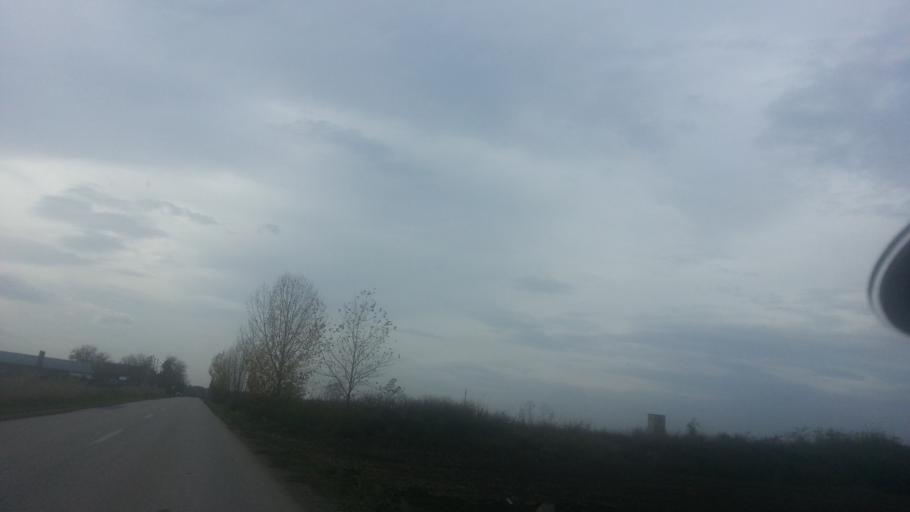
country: RS
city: Putinci
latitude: 44.9910
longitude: 19.9907
